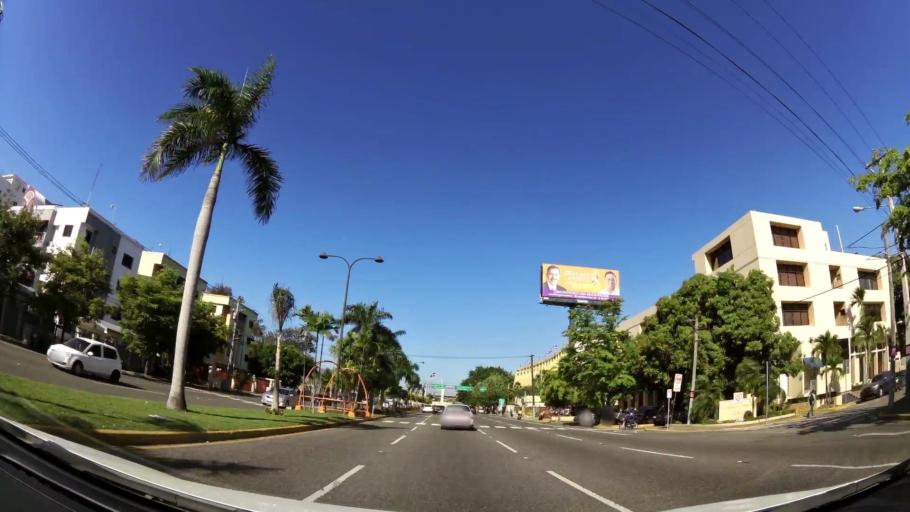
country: DO
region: Nacional
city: Bella Vista
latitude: 18.4499
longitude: -69.9707
